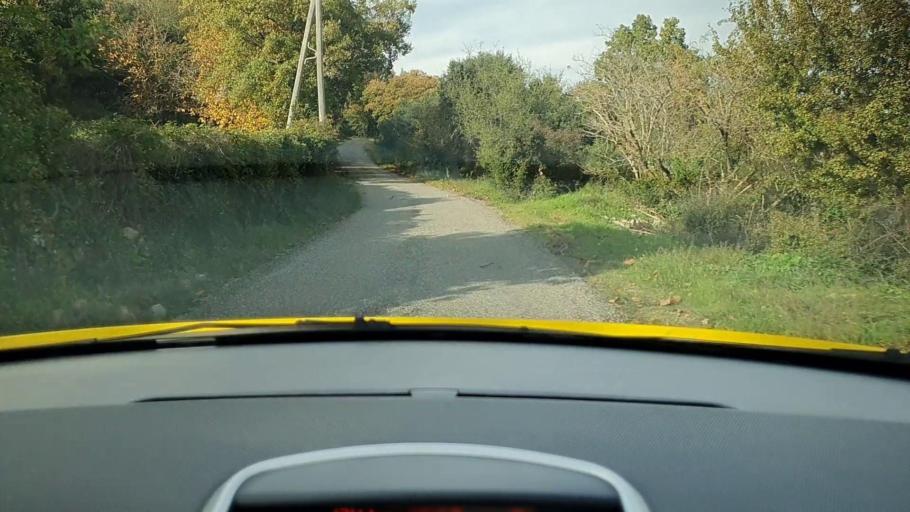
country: FR
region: Languedoc-Roussillon
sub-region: Departement du Gard
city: Anduze
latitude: 44.0353
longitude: 3.9275
